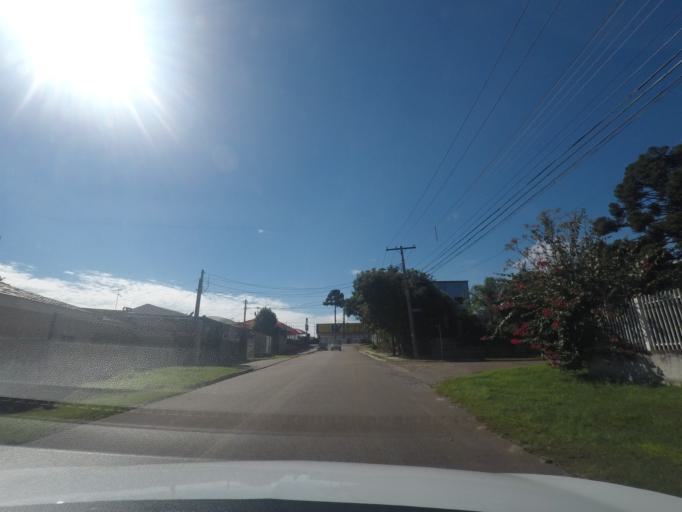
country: BR
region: Parana
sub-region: Sao Jose Dos Pinhais
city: Sao Jose dos Pinhais
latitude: -25.5033
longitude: -49.2661
